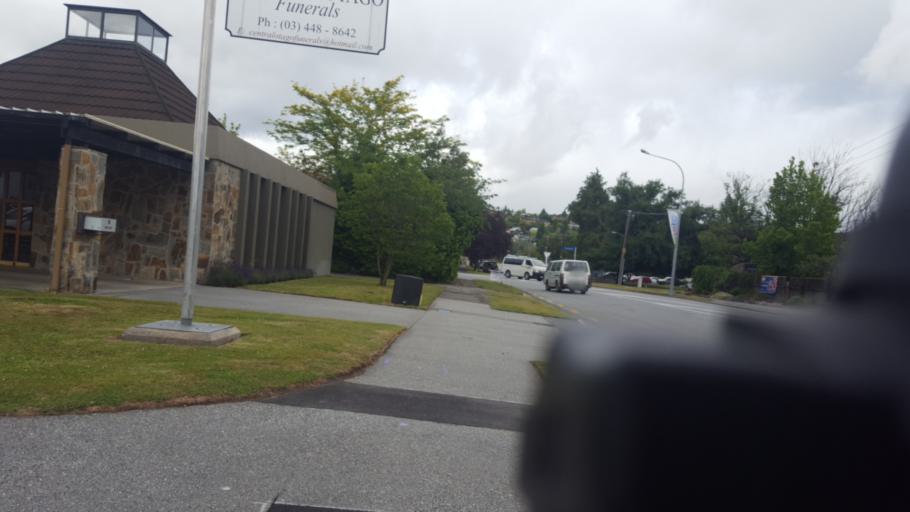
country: NZ
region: Otago
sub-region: Queenstown-Lakes District
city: Wanaka
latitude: -45.2558
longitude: 169.3913
